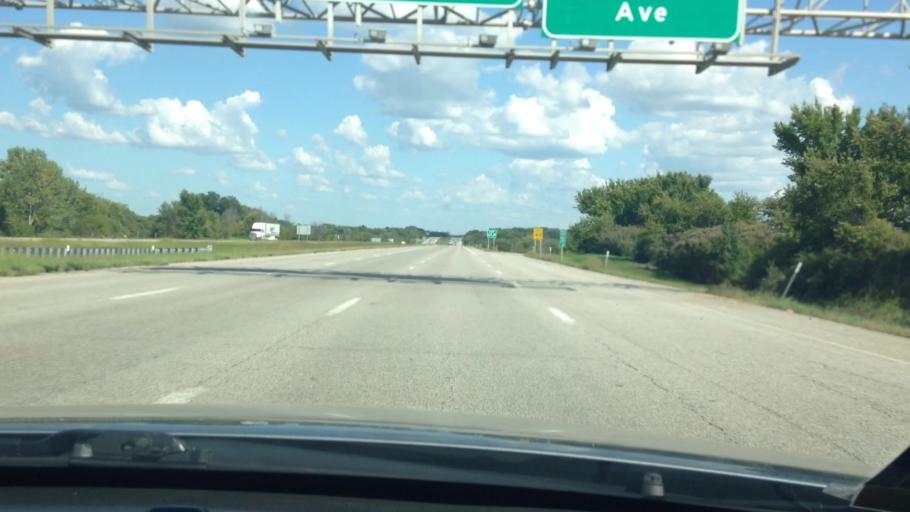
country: US
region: Missouri
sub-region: Platte County
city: Weatherby Lake
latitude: 39.3073
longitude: -94.6561
